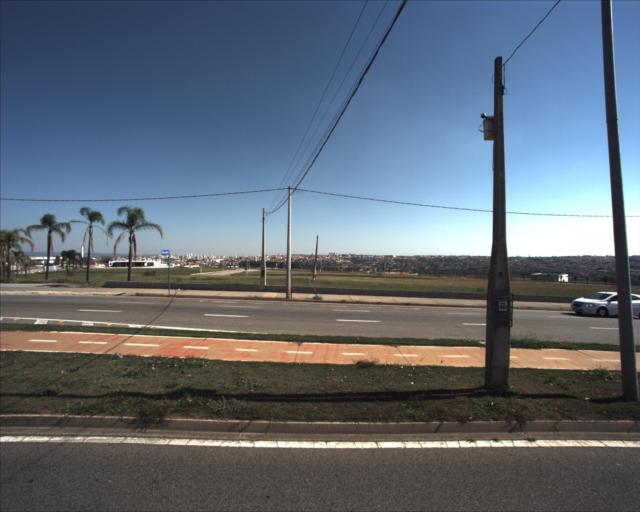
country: BR
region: Sao Paulo
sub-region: Sorocaba
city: Sorocaba
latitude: -23.4548
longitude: -47.4523
